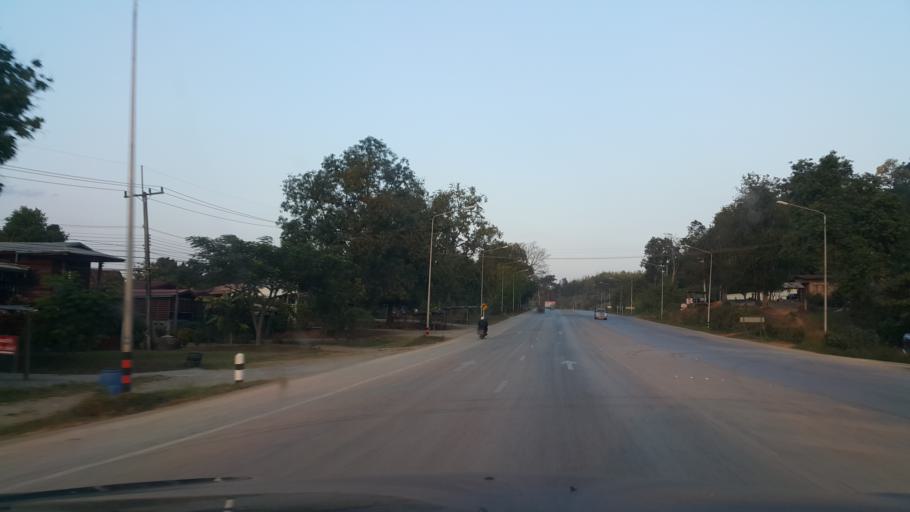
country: TH
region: Loei
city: Loei
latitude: 17.4915
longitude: 101.6873
